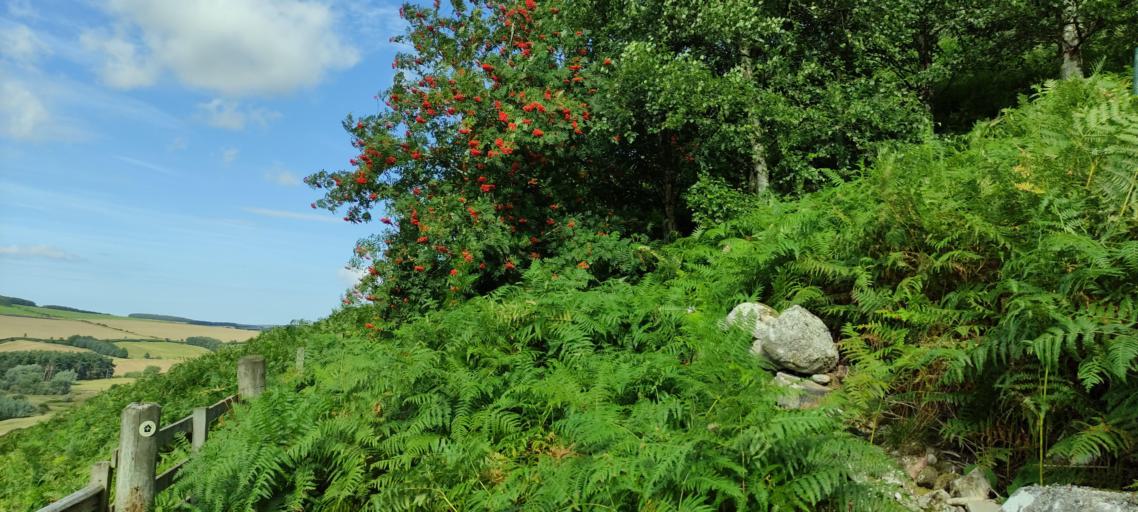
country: GB
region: England
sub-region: Northumberland
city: Doddington
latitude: 55.5562
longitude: -1.9716
